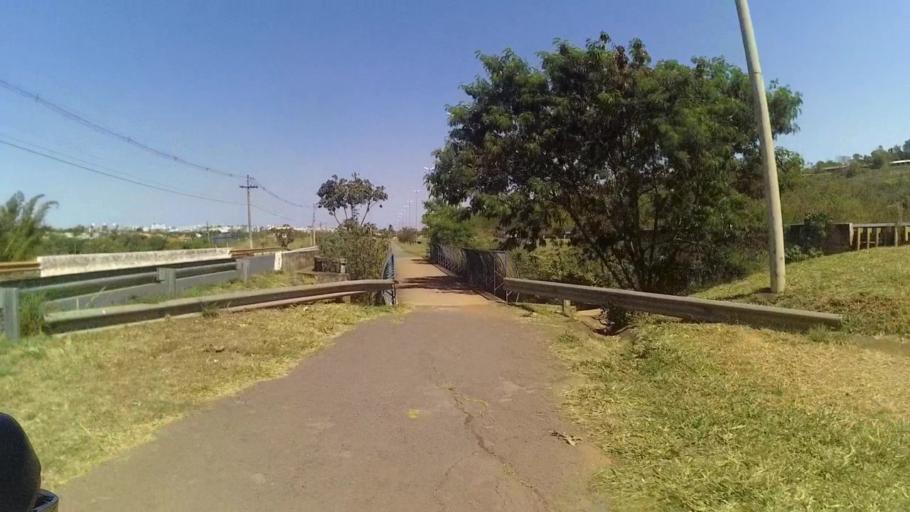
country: BR
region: Federal District
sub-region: Brasilia
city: Brasilia
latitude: -15.7176
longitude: -47.8641
